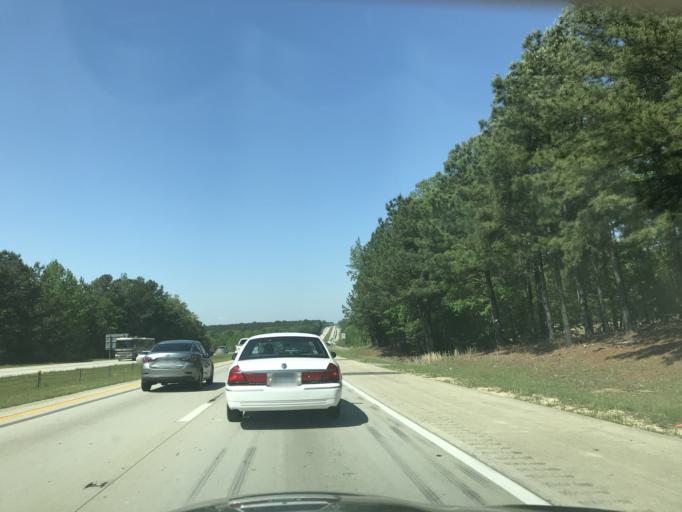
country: US
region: North Carolina
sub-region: Wake County
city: Garner
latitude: 35.6165
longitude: -78.5672
